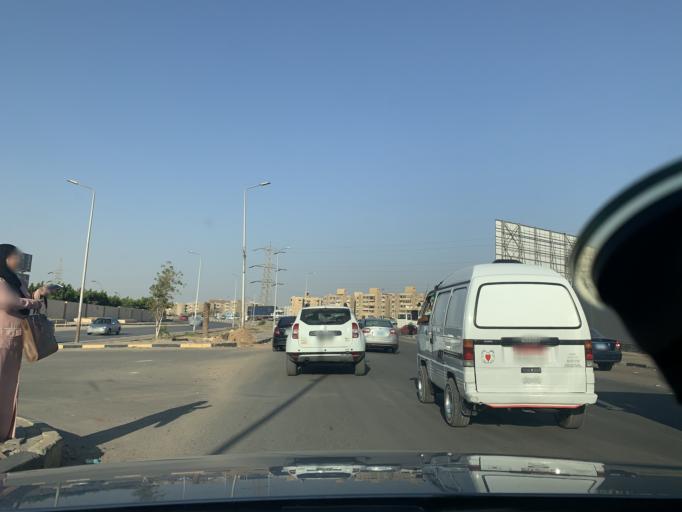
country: EG
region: Muhafazat al Qahirah
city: Cairo
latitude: 30.0356
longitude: 31.3528
